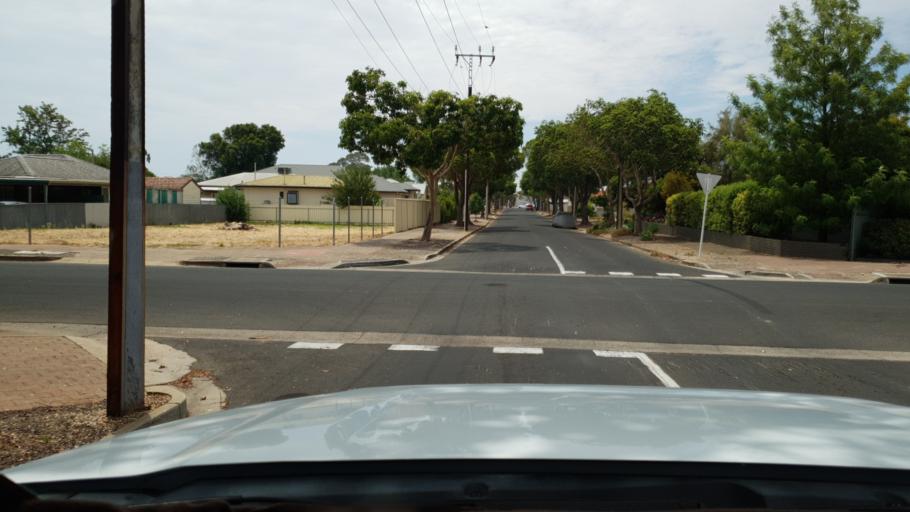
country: AU
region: South Australia
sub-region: Marion
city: Clovelly Park
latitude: -34.9948
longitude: 138.5800
